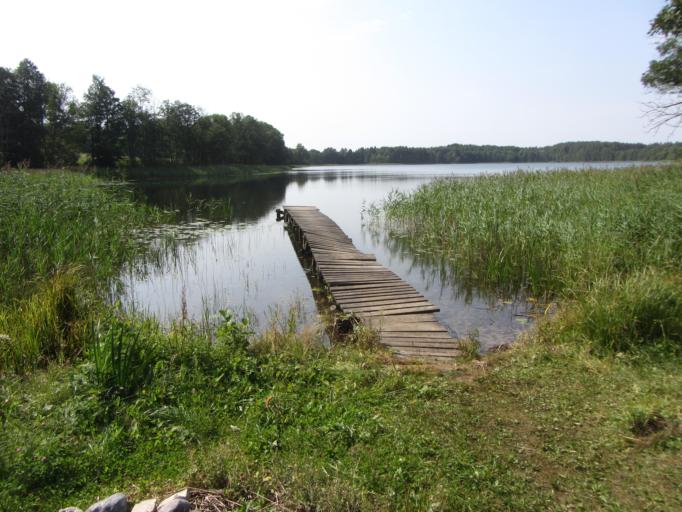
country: LT
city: Veisiejai
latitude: 54.0752
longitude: 23.7843
